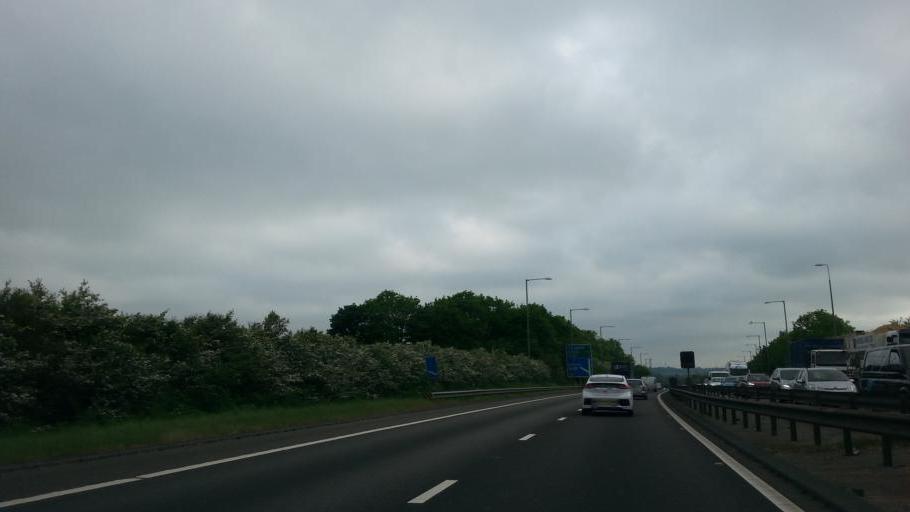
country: GB
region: England
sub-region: Doncaster
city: Marr
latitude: 53.5725
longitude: -1.2173
